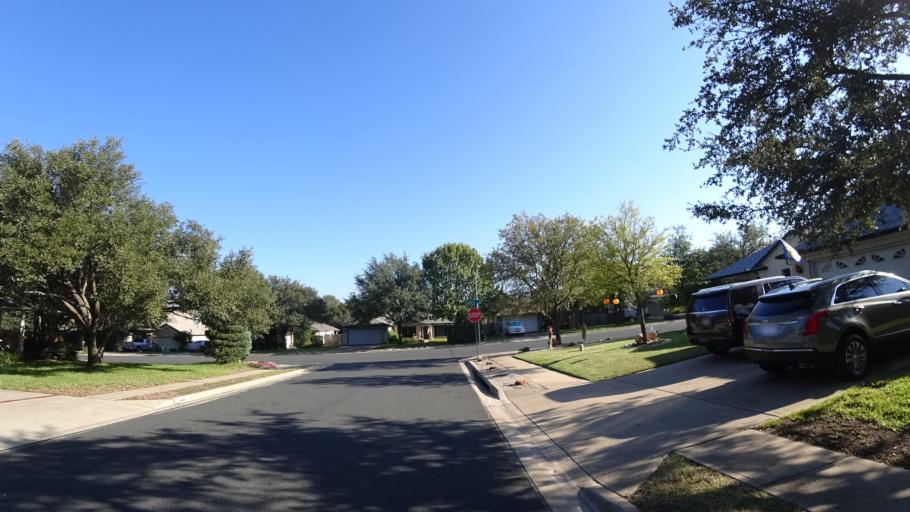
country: US
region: Texas
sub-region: Travis County
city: Shady Hollow
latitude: 30.2023
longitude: -97.8572
